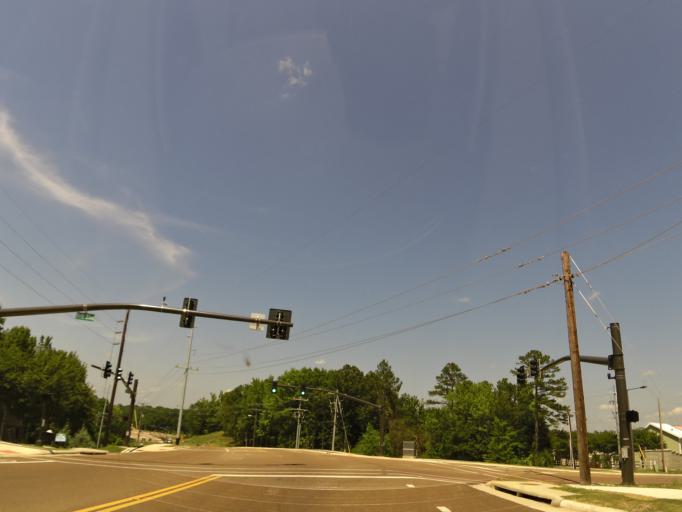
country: US
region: Mississippi
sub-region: Lafayette County
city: University
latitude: 34.3512
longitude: -89.5346
